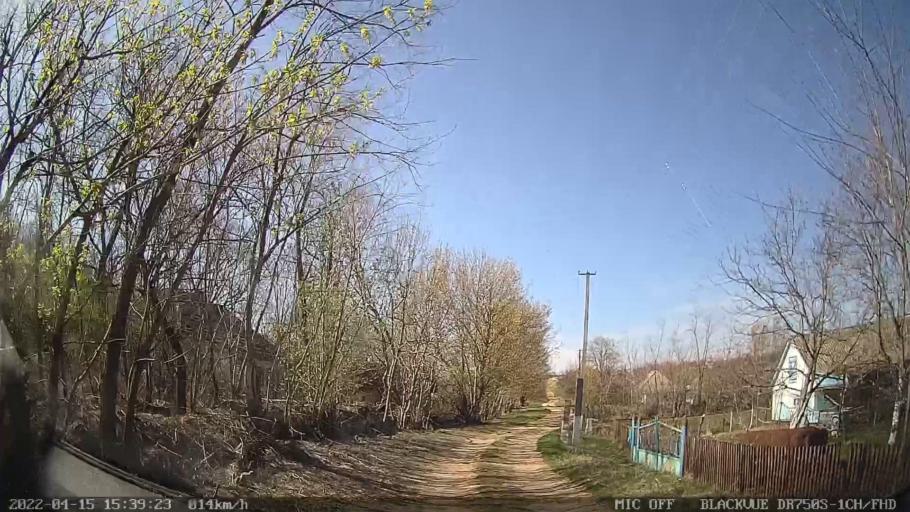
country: MD
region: Raionul Ocnita
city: Otaci
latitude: 48.3534
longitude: 27.9273
